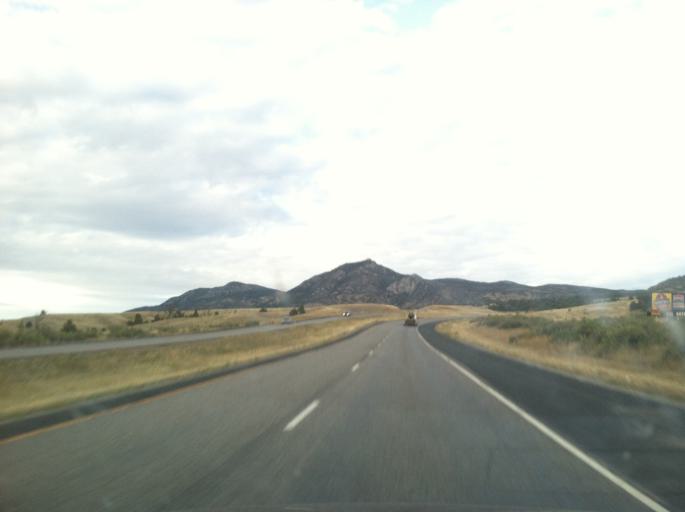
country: US
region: Montana
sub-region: Jefferson County
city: Whitehall
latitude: 45.8727
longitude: -111.9356
